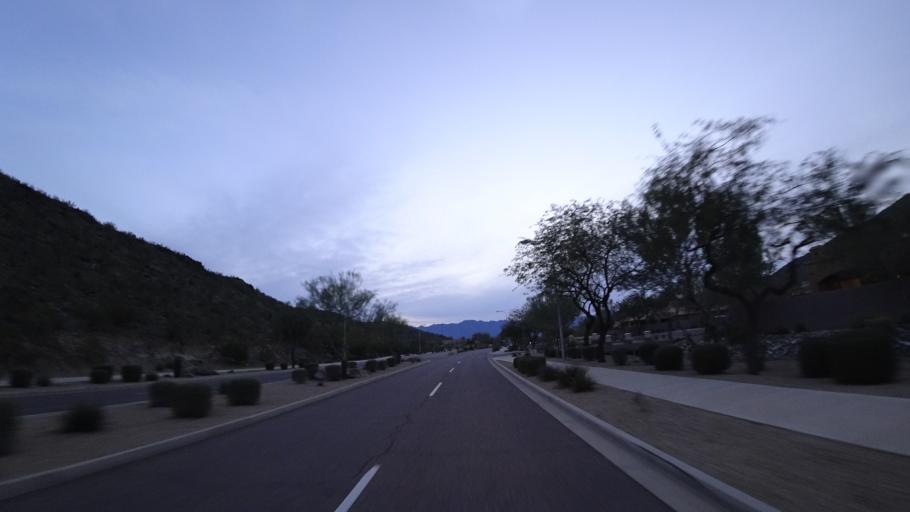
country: US
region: Arizona
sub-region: Maricopa County
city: Laveen
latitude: 33.3135
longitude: -112.0731
